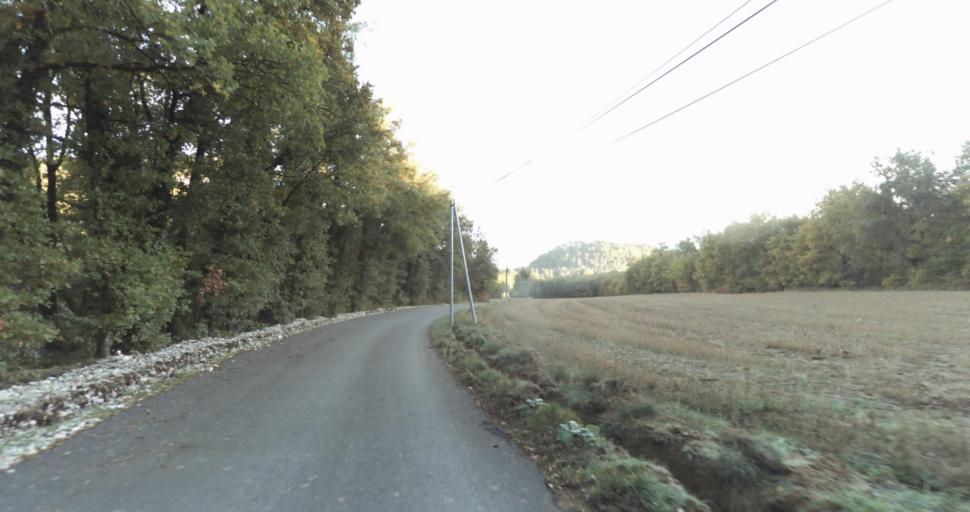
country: FR
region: Provence-Alpes-Cote d'Azur
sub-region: Departement des Bouches-du-Rhone
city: Venelles
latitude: 43.5942
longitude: 5.5167
